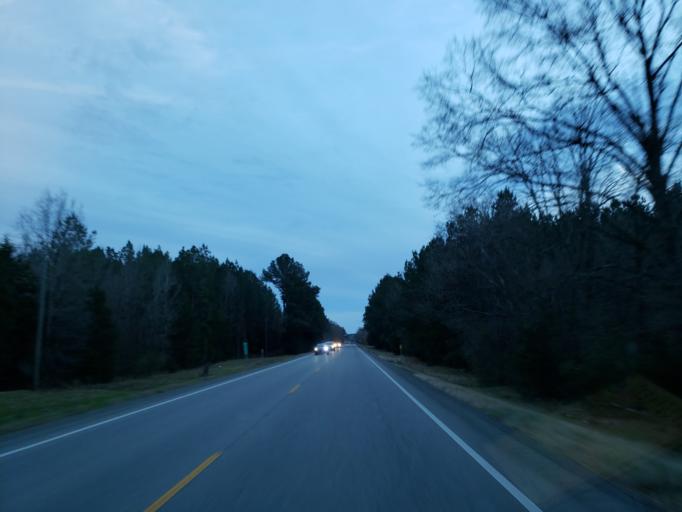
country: US
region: Alabama
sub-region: Sumter County
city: Livingston
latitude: 32.8153
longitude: -88.3111
